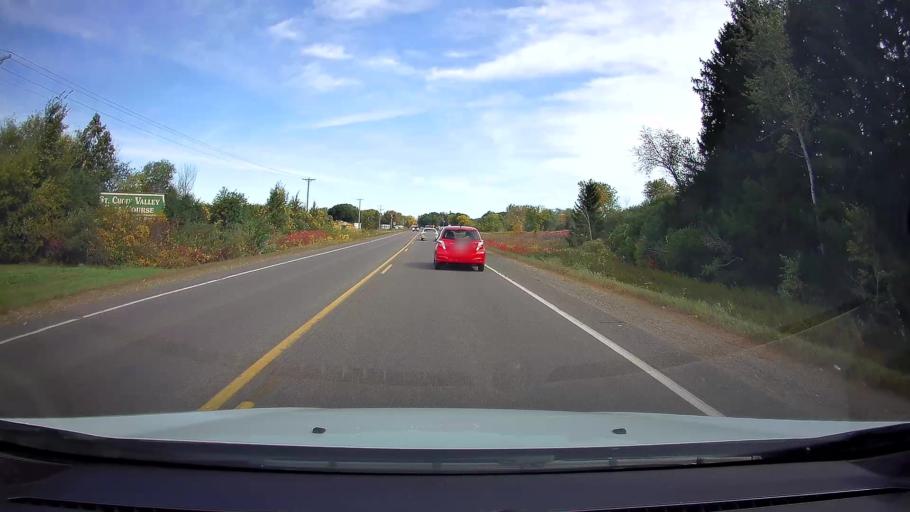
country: US
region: Wisconsin
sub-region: Polk County
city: Saint Croix Falls
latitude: 45.3463
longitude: -92.6407
